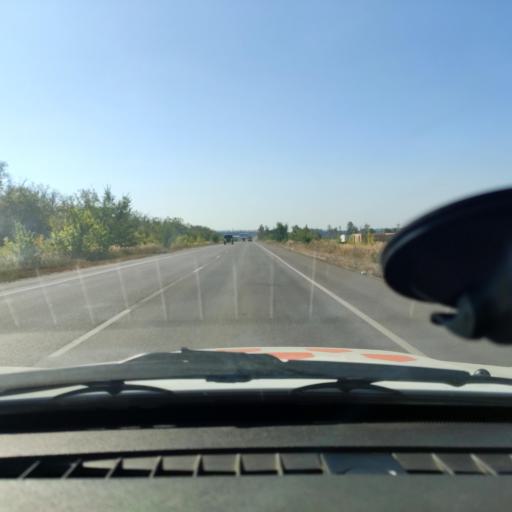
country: RU
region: Voronezj
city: Novaya Usman'
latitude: 51.6126
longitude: 39.3368
